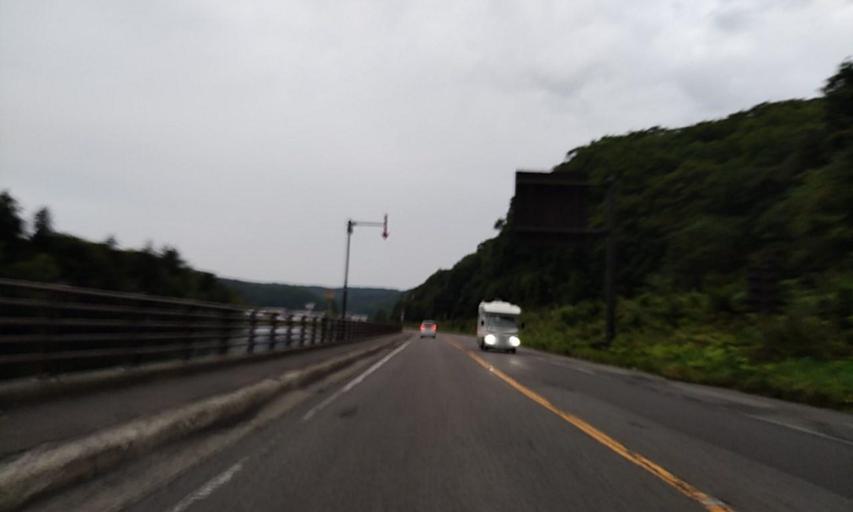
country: JP
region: Hokkaido
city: Abashiri
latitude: 44.0062
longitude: 144.2315
